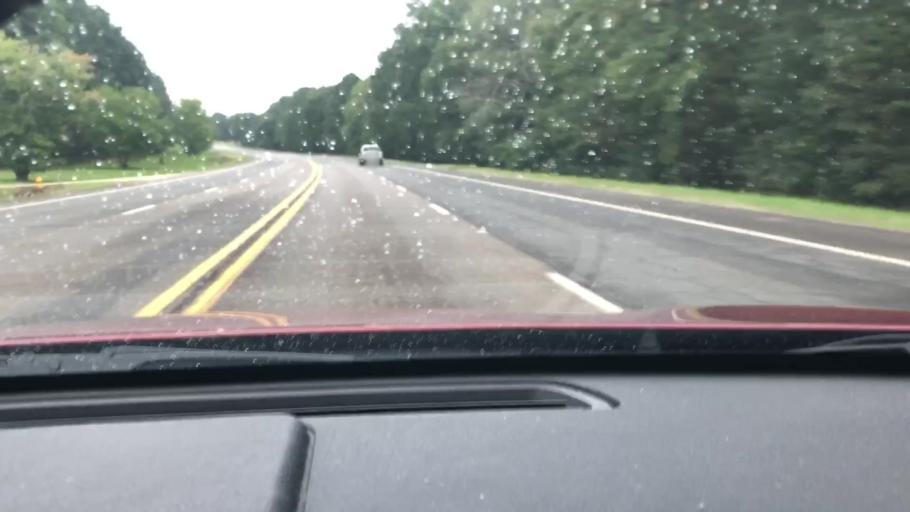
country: US
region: Arkansas
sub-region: Lafayette County
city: Lewisville
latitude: 33.3553
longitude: -93.5665
